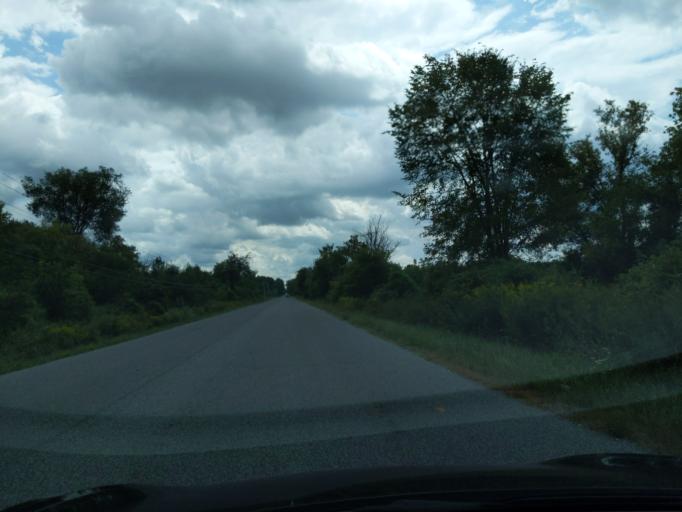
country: US
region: Michigan
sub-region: Eaton County
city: Dimondale
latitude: 42.6532
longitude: -84.5826
